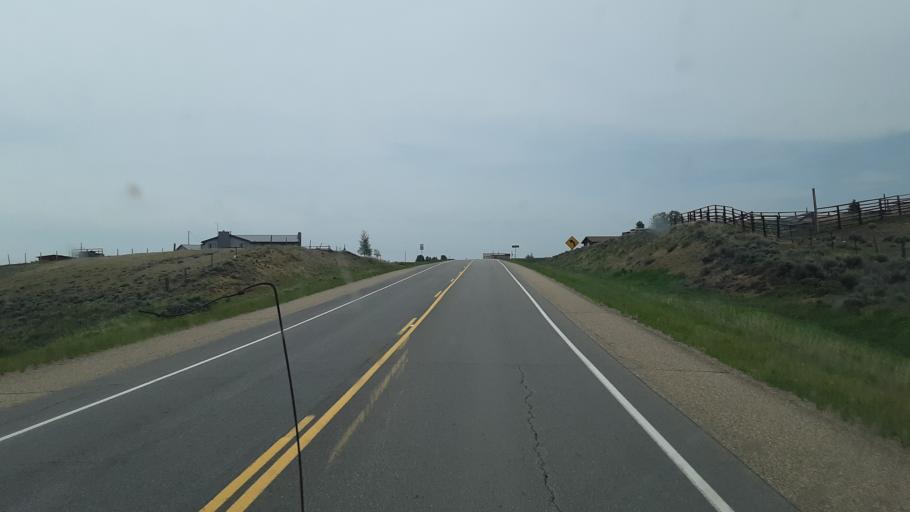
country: US
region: Colorado
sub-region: Jackson County
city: Walden
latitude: 40.8631
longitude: -106.3119
